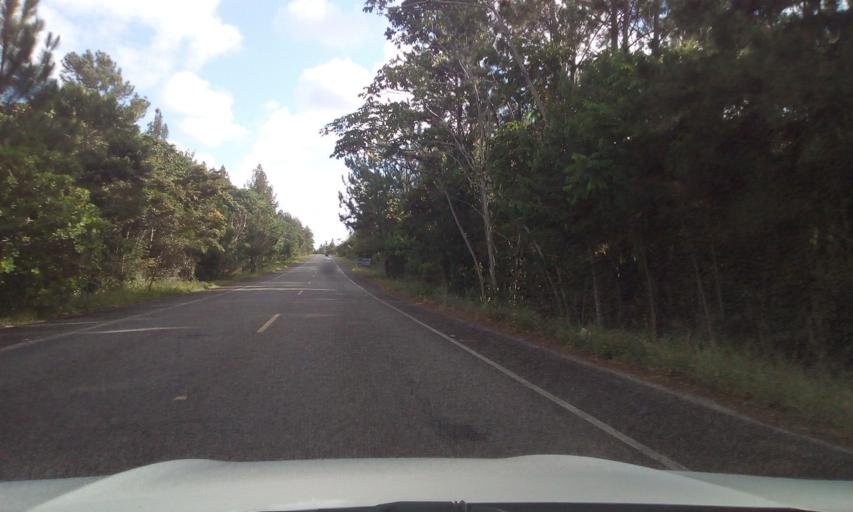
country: BR
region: Bahia
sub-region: Entre Rios
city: Entre Rios
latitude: -12.1469
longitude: -37.7962
